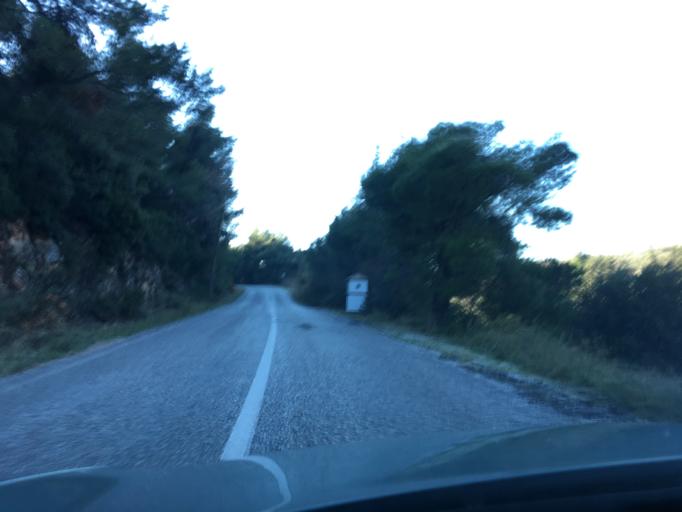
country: GR
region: Thessaly
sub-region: Nomos Magnisias
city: Skopelos
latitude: 39.1022
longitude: 23.7010
